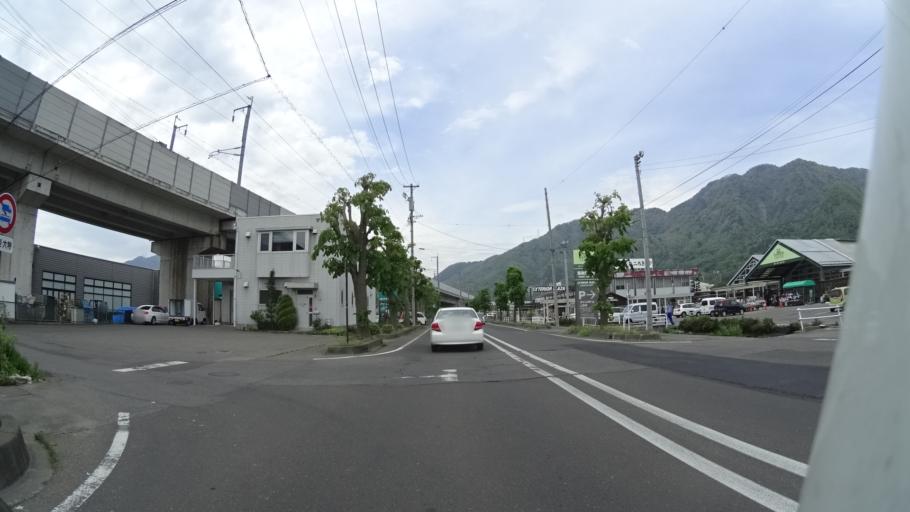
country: JP
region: Nagano
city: Ueda
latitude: 36.4102
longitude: 138.2285
